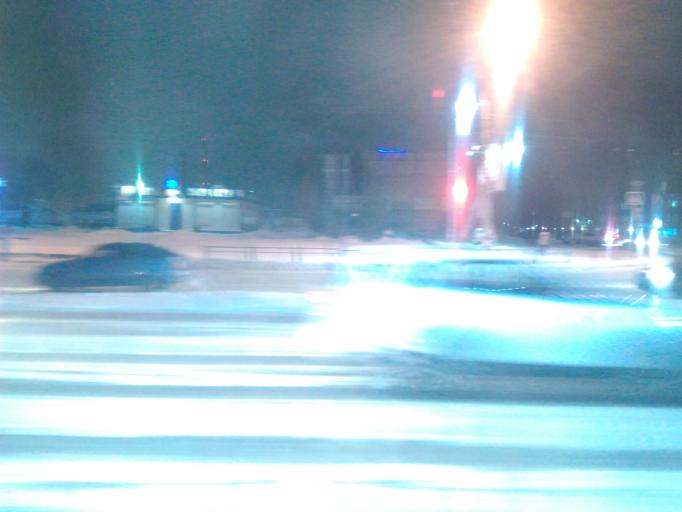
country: RU
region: Ulyanovsk
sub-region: Ulyanovskiy Rayon
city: Ulyanovsk
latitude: 54.3216
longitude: 48.3567
